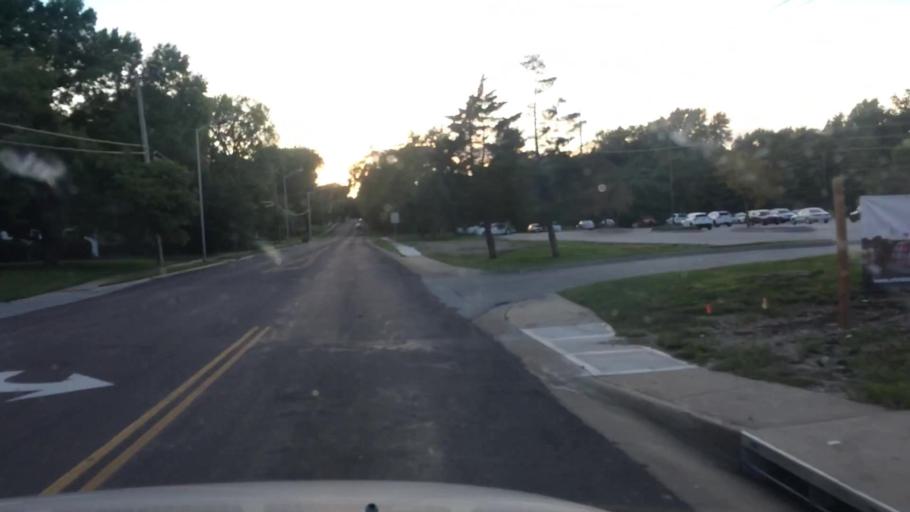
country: US
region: Kansas
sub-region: Johnson County
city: Overland Park
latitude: 38.9641
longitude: -94.6488
